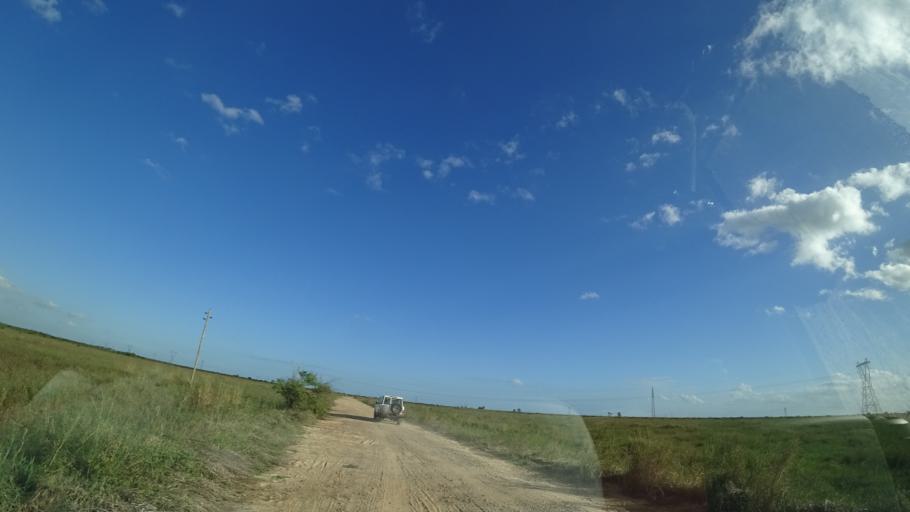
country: MZ
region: Sofala
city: Dondo
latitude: -19.4566
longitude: 34.5630
